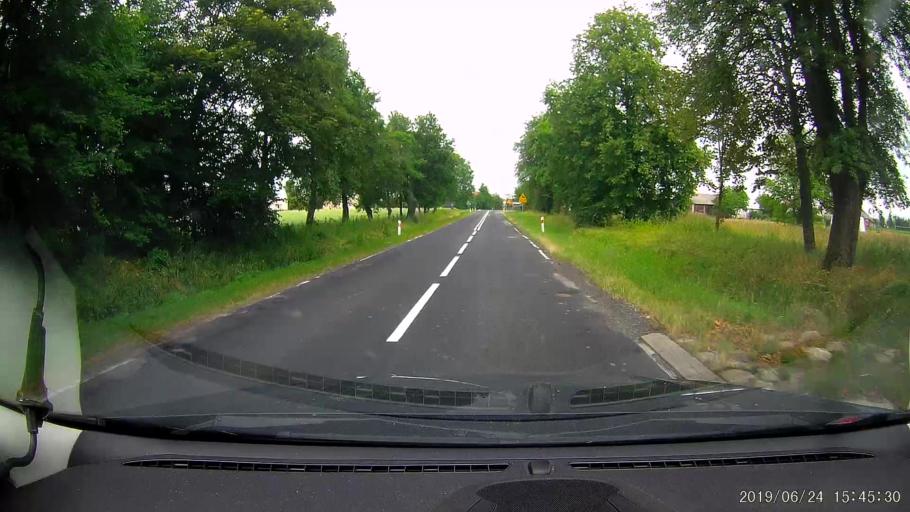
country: PL
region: Subcarpathian Voivodeship
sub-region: Powiat lubaczowski
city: Oleszyce
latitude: 50.1488
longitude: 22.9828
